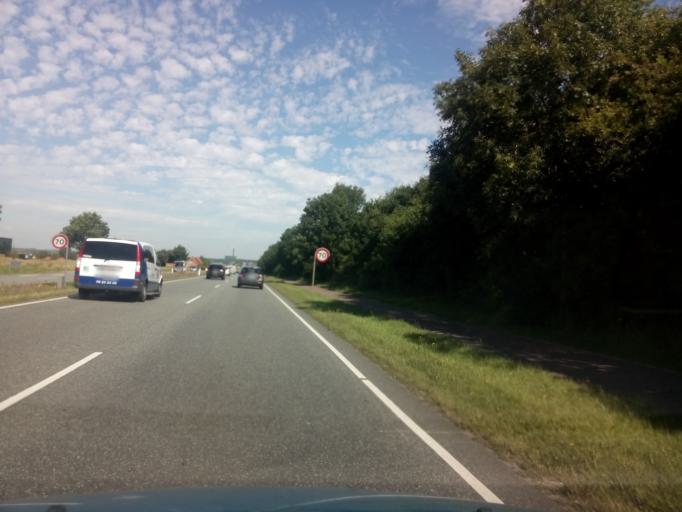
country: DK
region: Central Jutland
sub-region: Arhus Kommune
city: Arhus
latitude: 56.1962
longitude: 10.1849
